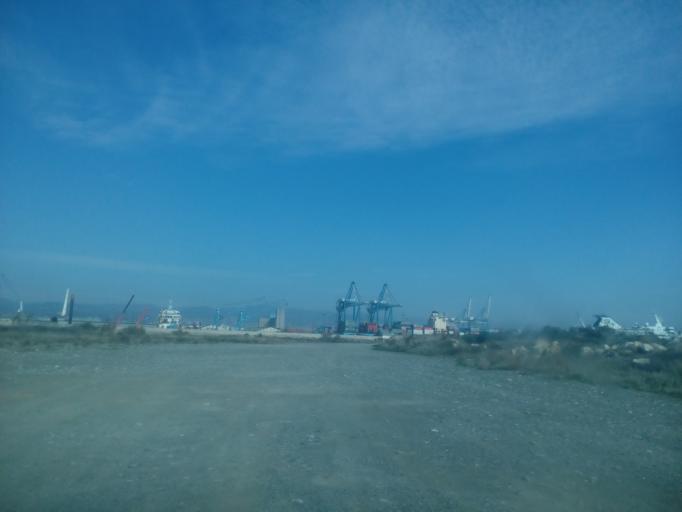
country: CY
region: Limassol
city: Limassol
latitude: 34.6414
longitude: 33.0107
